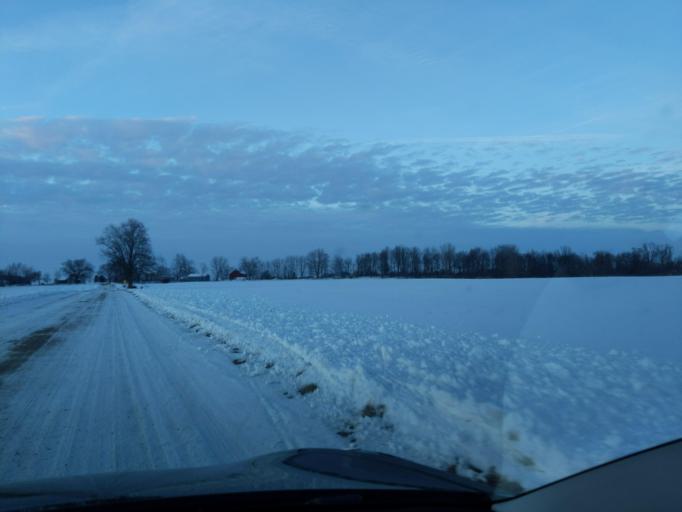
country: US
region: Michigan
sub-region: Ingham County
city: Williamston
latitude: 42.5725
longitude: -84.3157
